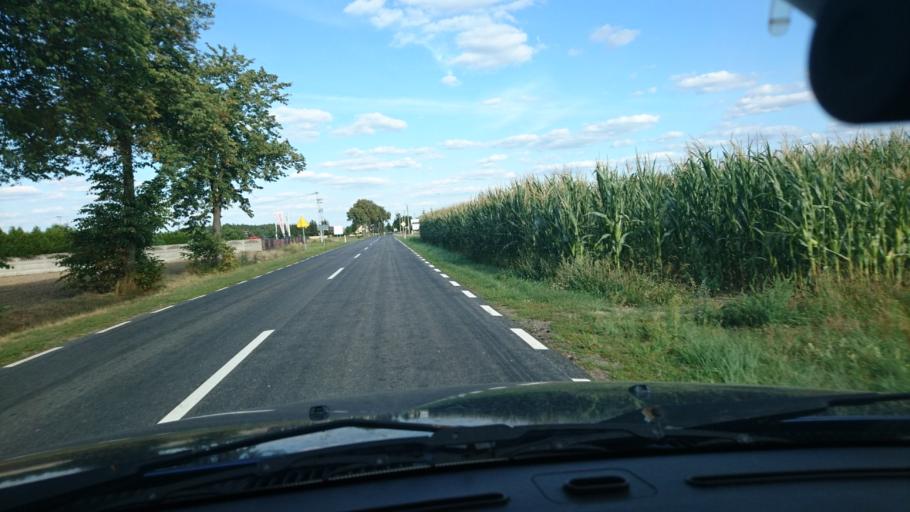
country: PL
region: Greater Poland Voivodeship
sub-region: Powiat krotoszynski
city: Sulmierzyce
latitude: 51.6154
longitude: 17.5058
